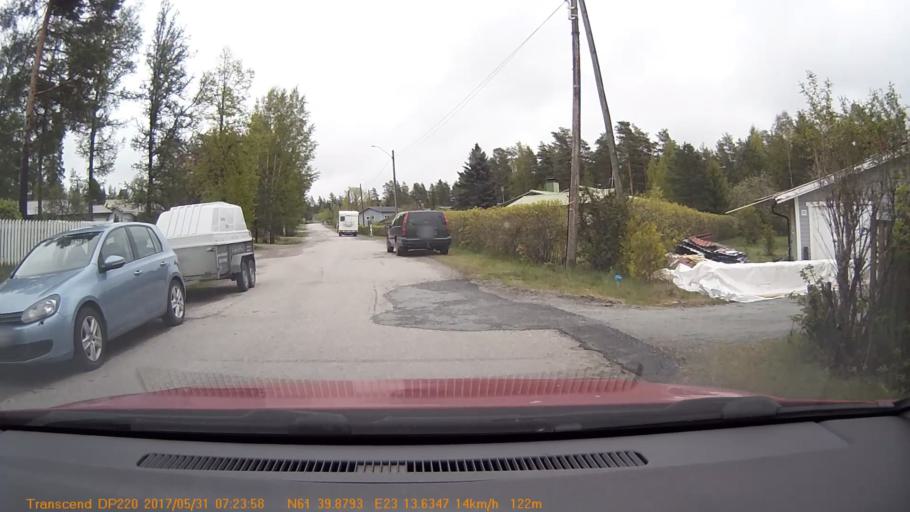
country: FI
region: Pirkanmaa
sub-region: Tampere
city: Haemeenkyroe
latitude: 61.6647
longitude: 23.2272
